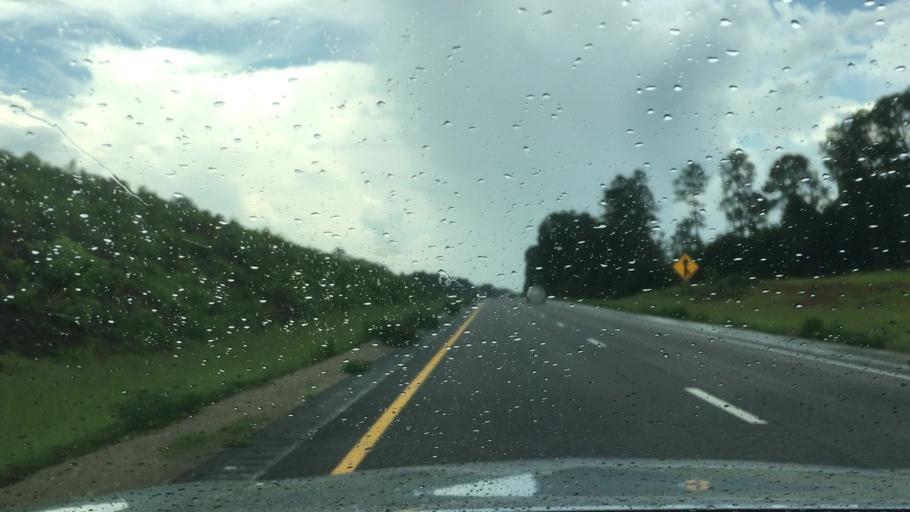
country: US
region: Mississippi
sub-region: Lamar County
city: Purvis
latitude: 31.2022
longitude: -89.3366
